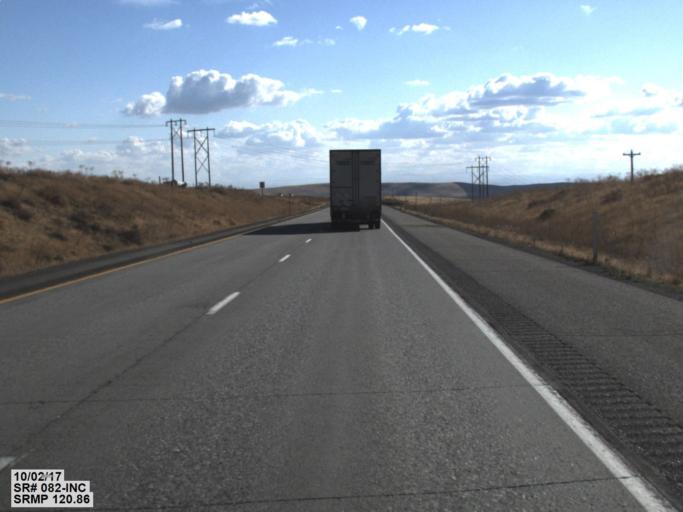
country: US
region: Washington
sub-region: Benton County
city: Highland
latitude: 46.0528
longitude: -119.2244
